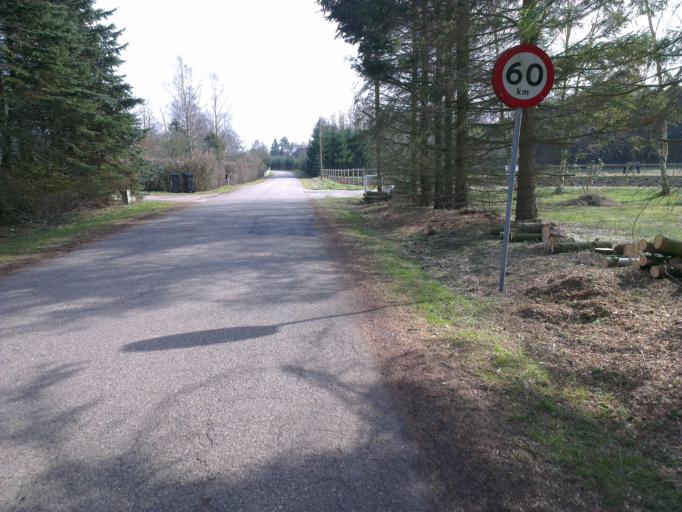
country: DK
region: Capital Region
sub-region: Egedal Kommune
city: Olstykke
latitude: 55.7907
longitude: 12.1745
